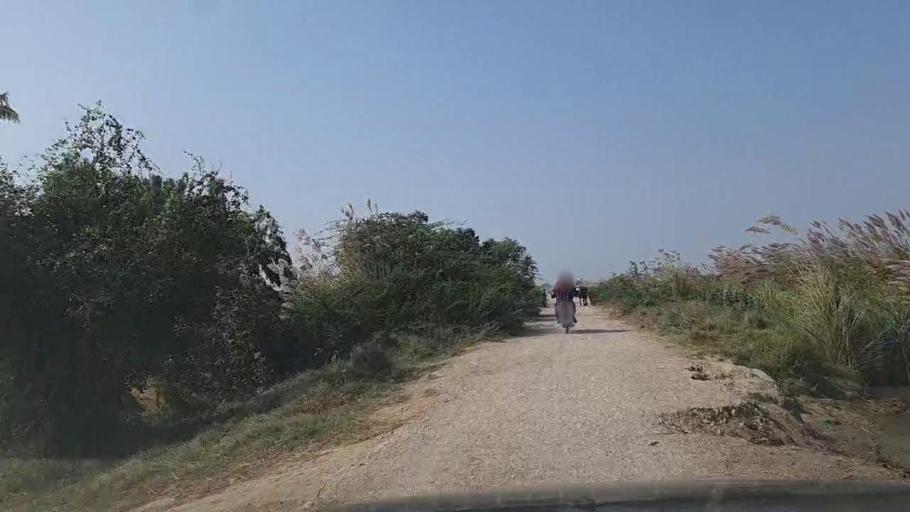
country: PK
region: Sindh
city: Gharo
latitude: 24.7028
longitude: 67.6370
